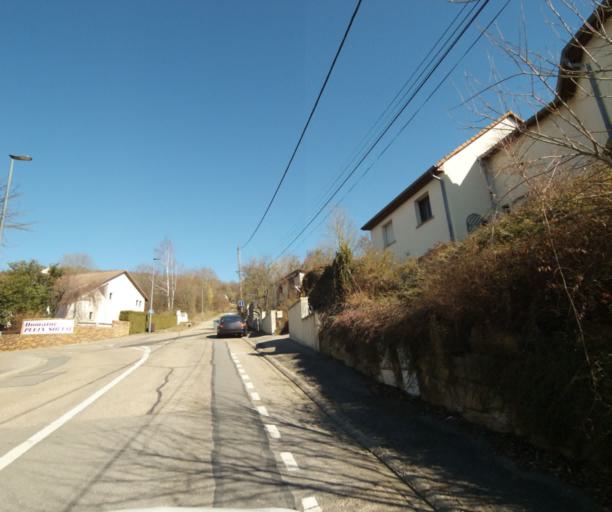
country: FR
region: Lorraine
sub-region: Departement de Meurthe-et-Moselle
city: Essey-les-Nancy
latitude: 48.7115
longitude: 6.2231
